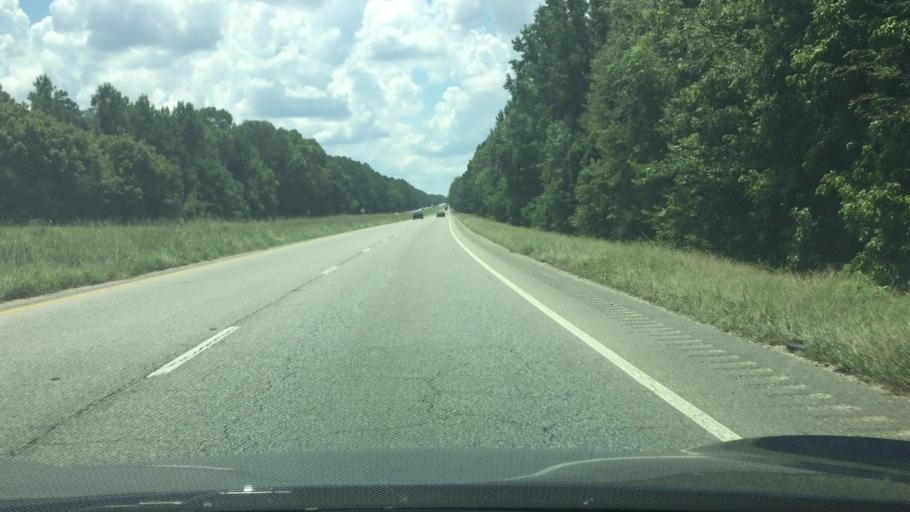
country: US
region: Alabama
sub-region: Montgomery County
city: Pike Road
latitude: 32.1102
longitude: -86.0663
